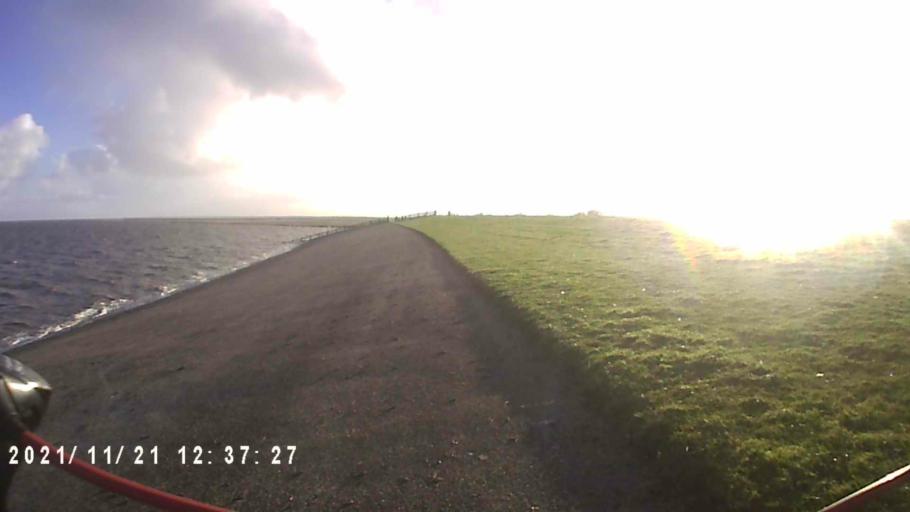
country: NL
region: Friesland
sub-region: Gemeente Dongeradeel
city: Anjum
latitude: 53.4064
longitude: 6.0726
